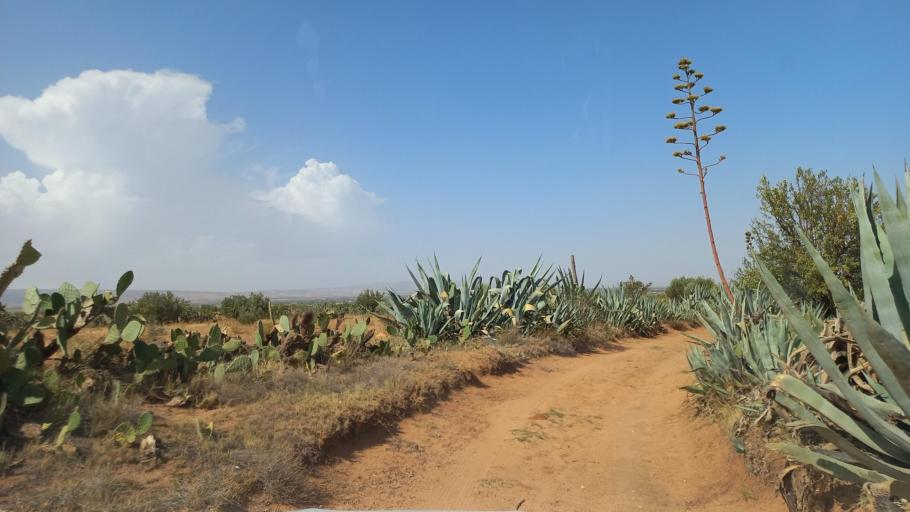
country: TN
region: Al Qasrayn
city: Kasserine
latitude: 35.2044
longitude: 9.0194
